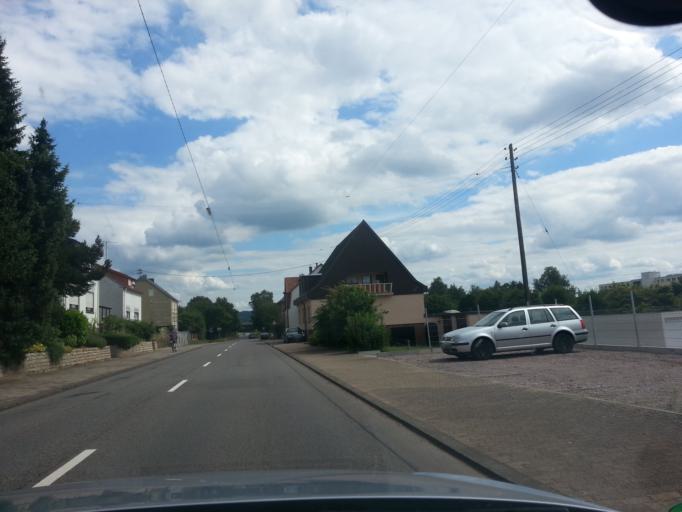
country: DE
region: Saarland
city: Mettlach
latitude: 49.4684
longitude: 6.6150
